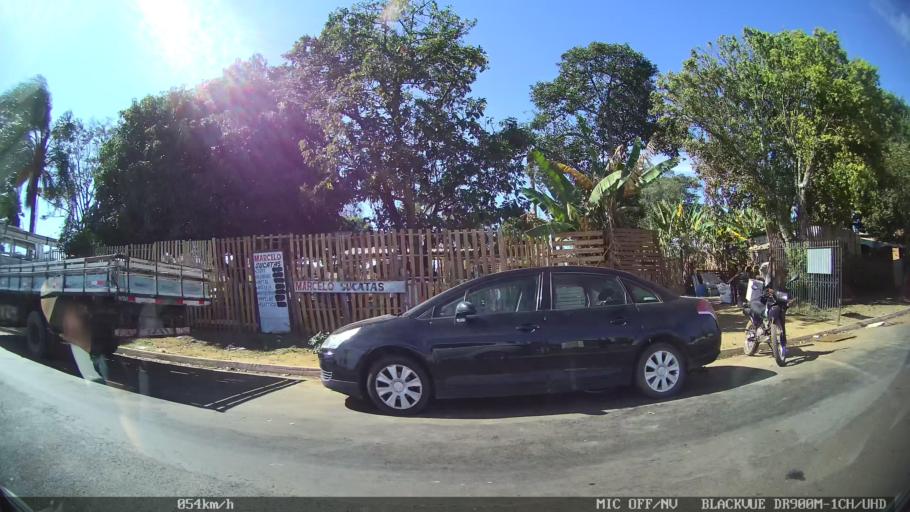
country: BR
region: Sao Paulo
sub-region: Franca
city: Franca
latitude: -20.4857
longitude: -47.3998
